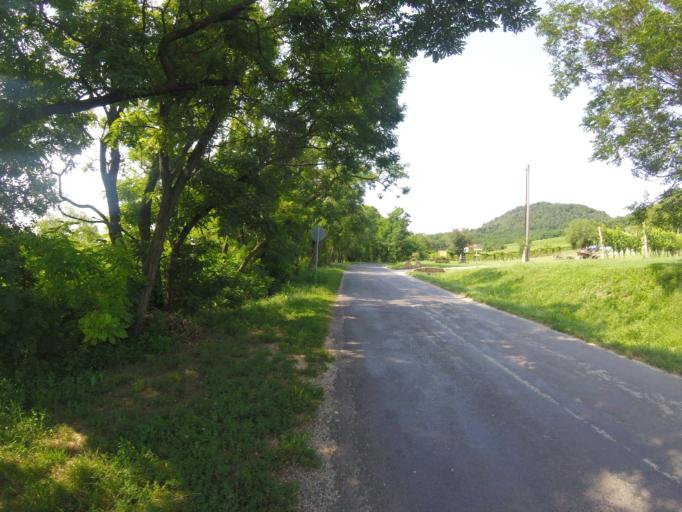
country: HU
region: Veszprem
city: Badacsonytomaj
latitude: 46.8051
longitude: 17.4588
